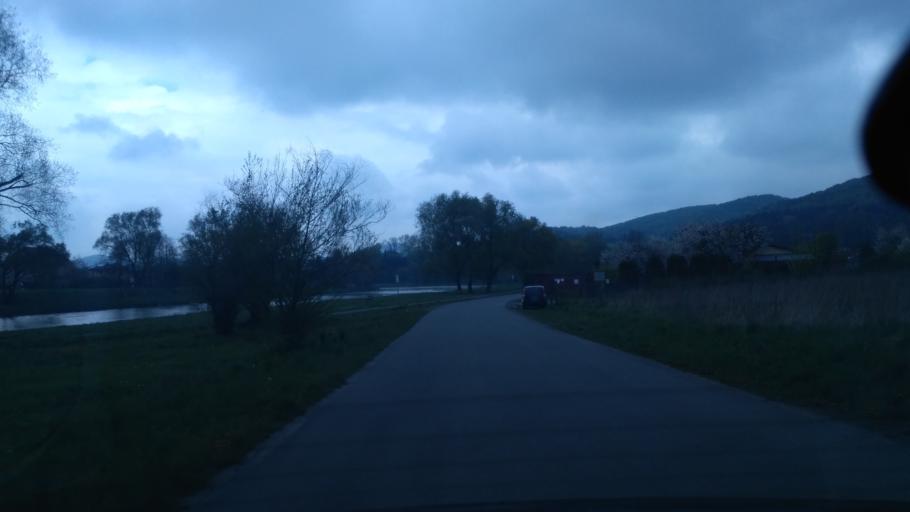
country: PL
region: Subcarpathian Voivodeship
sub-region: Powiat sanocki
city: Sanok
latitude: 49.5680
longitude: 22.2088
